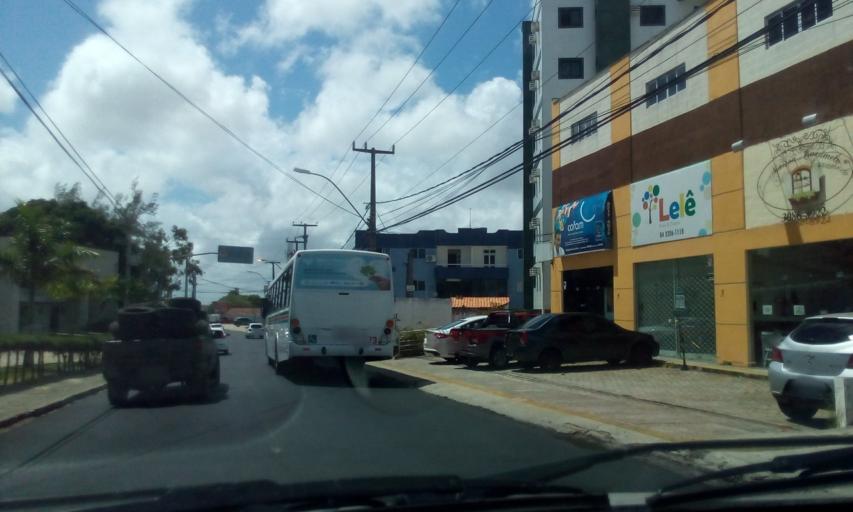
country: BR
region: Rio Grande do Norte
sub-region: Natal
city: Natal
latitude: -5.8535
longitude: -35.2060
